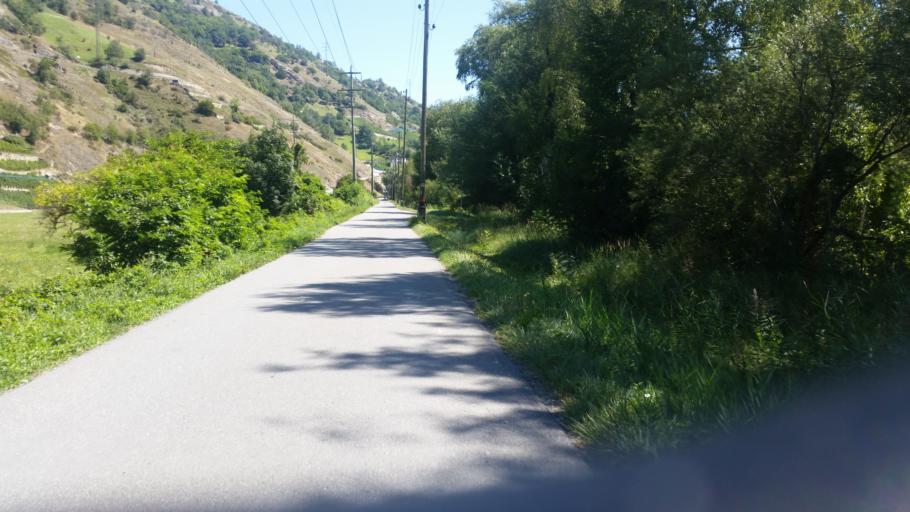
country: CH
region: Valais
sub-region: Raron District
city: Raron
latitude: 46.3083
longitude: 7.8231
